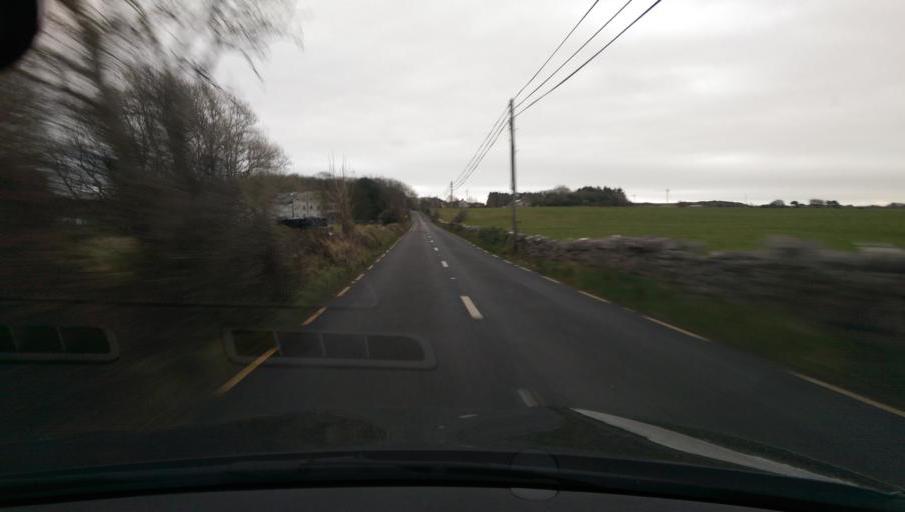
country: IE
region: Connaught
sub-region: County Galway
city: Athenry
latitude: 53.3098
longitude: -8.7944
